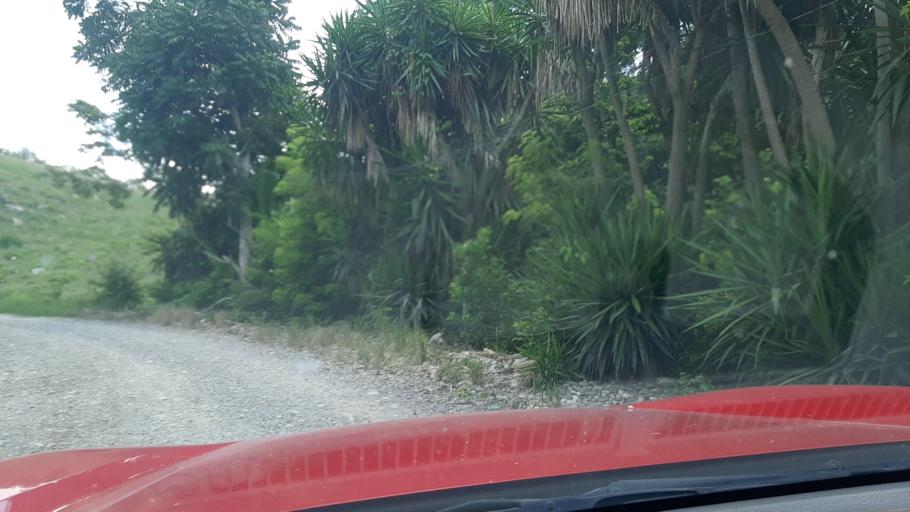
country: MX
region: Veracruz
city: Agua Dulce
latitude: 20.4157
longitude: -97.2789
